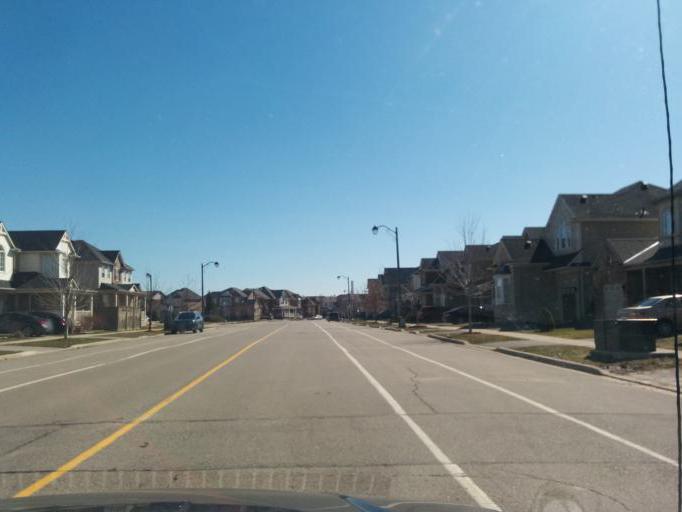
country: CA
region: Ontario
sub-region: Halton
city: Milton
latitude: 43.5075
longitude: -79.8456
